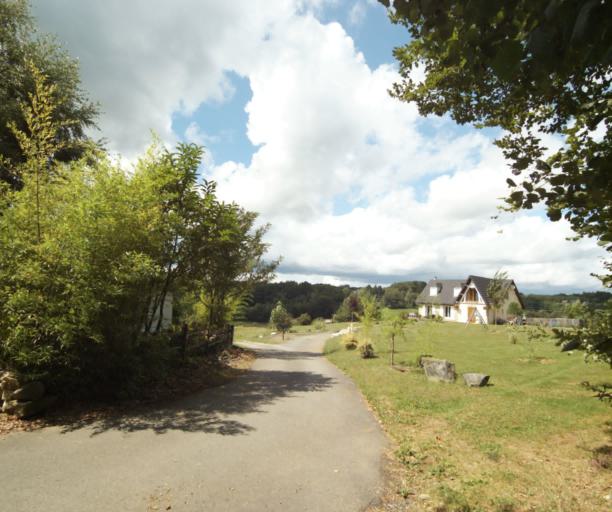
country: FR
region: Limousin
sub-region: Departement de la Correze
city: Sainte-Fortunade
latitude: 45.1743
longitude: 1.8259
